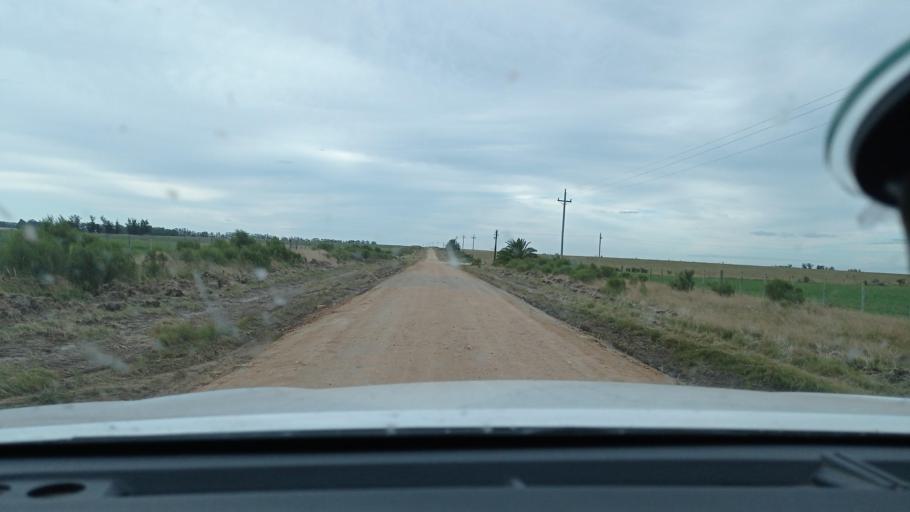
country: UY
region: Florida
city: Casupa
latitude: -34.1050
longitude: -55.7633
